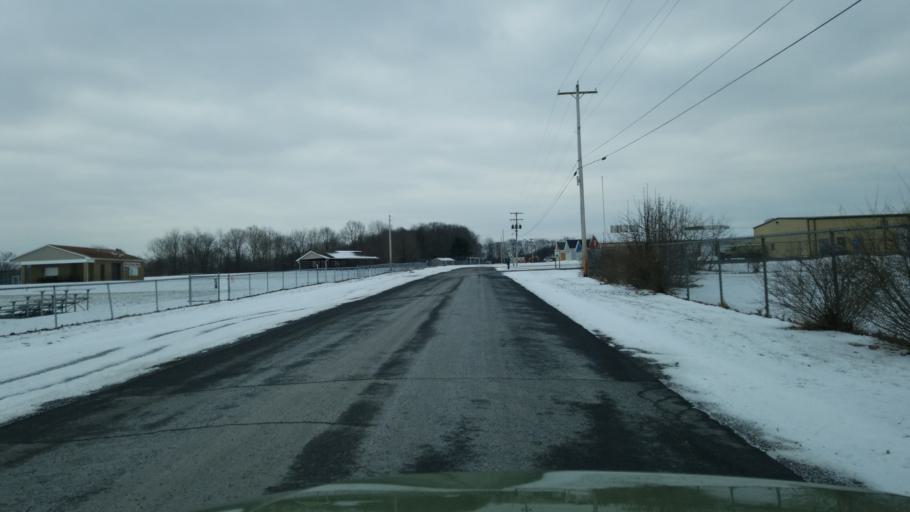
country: US
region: Pennsylvania
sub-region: Clearfield County
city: DuBois
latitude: 41.1096
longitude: -78.7313
